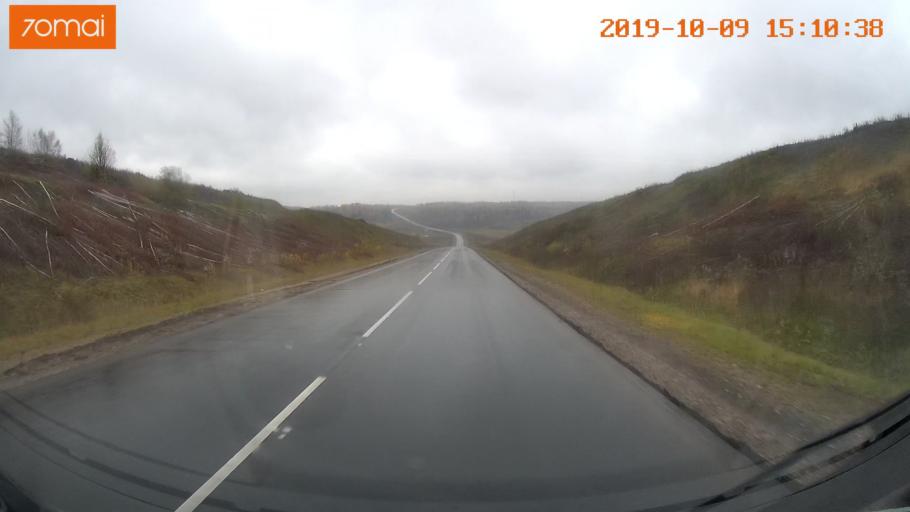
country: RU
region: Kostroma
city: Susanino
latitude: 58.1755
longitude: 41.6377
